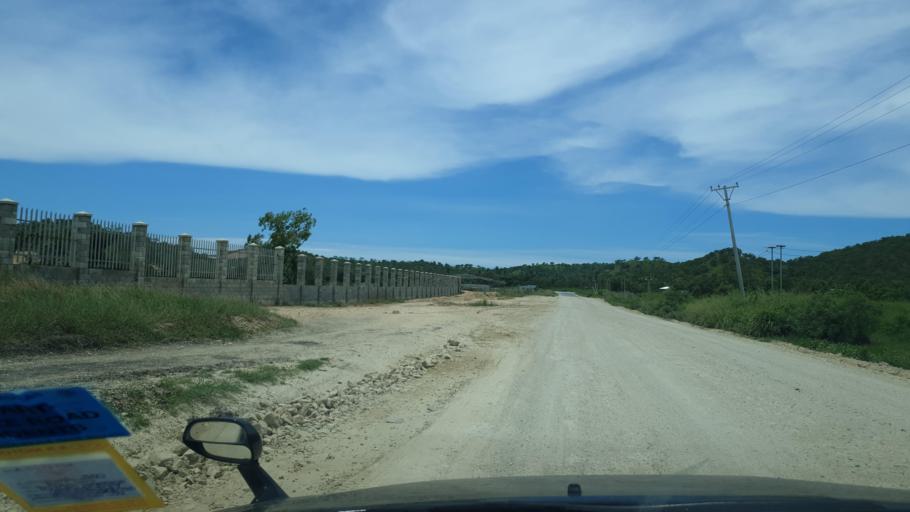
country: PG
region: National Capital
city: Port Moresby
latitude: -9.4206
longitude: 147.0769
